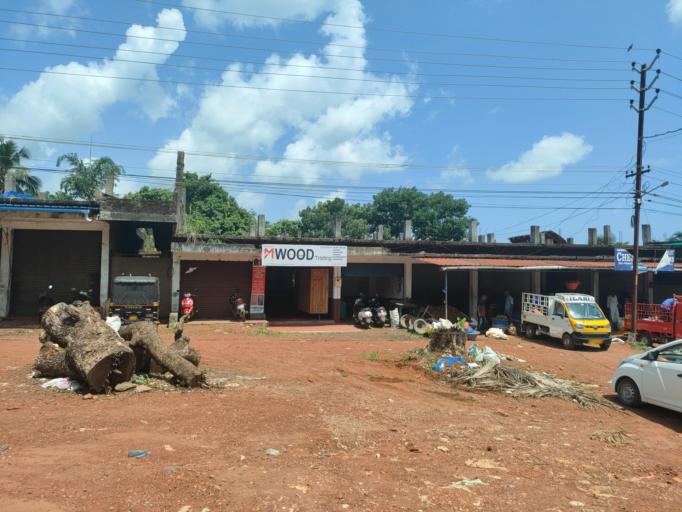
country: IN
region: Kerala
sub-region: Kasaragod District
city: Kasaragod
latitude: 12.5160
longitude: 75.0095
